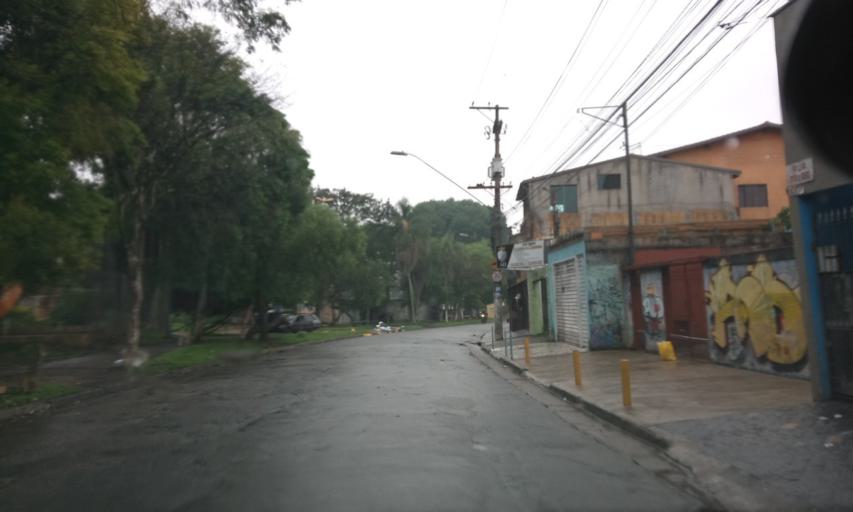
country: BR
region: Sao Paulo
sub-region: Santo Andre
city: Santo Andre
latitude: -23.7050
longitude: -46.5078
